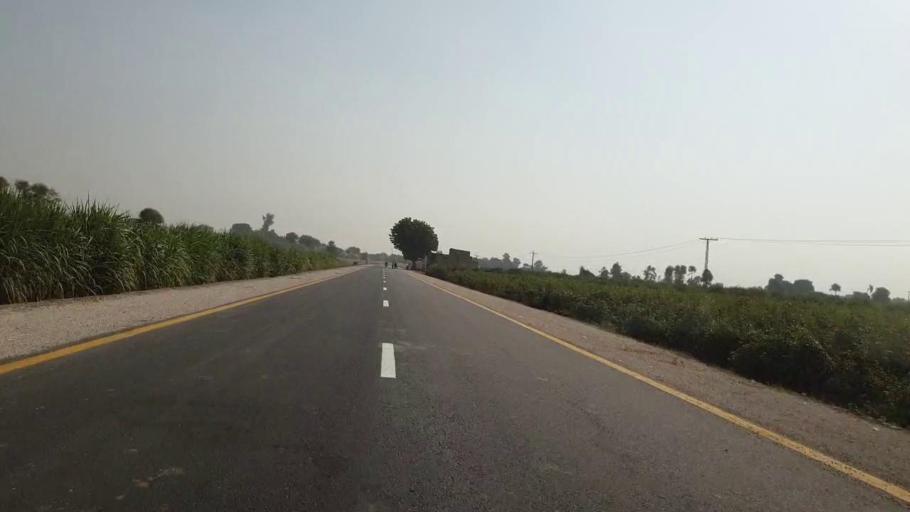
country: PK
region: Sindh
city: Bhan
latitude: 26.6060
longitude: 67.7791
